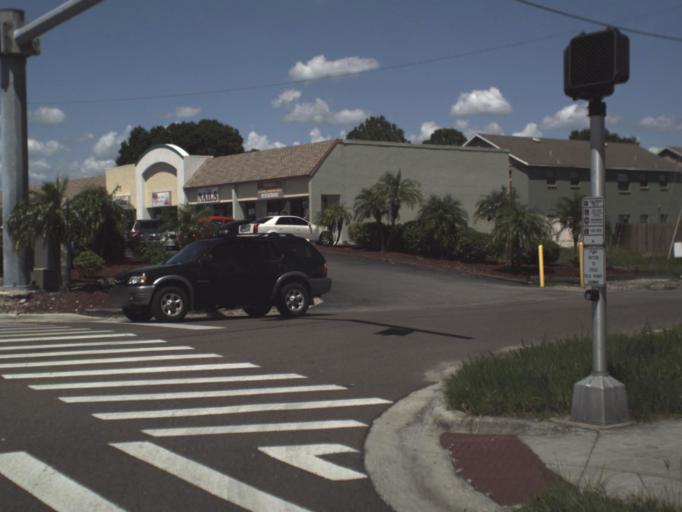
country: US
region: Florida
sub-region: Hillsborough County
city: Tampa
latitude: 27.8899
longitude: -82.5063
